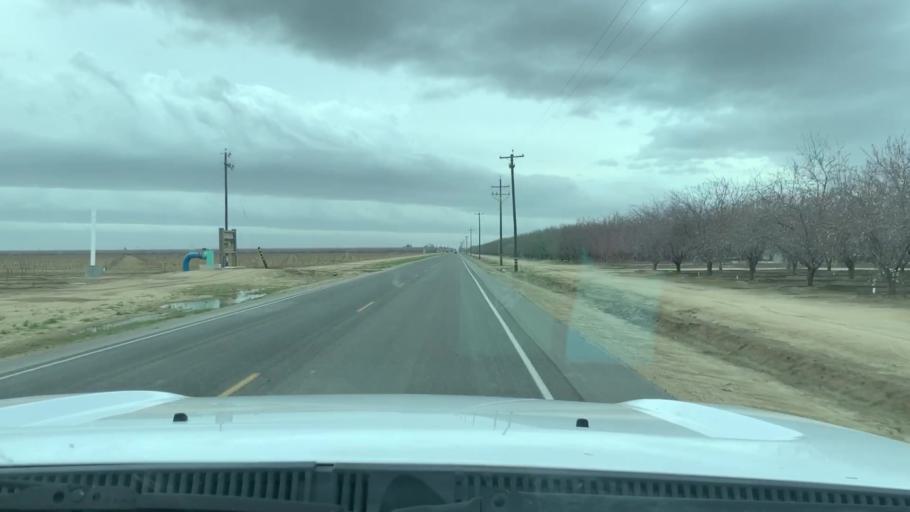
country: US
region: California
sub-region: Kern County
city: Wasco
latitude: 35.5581
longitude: -119.3036
